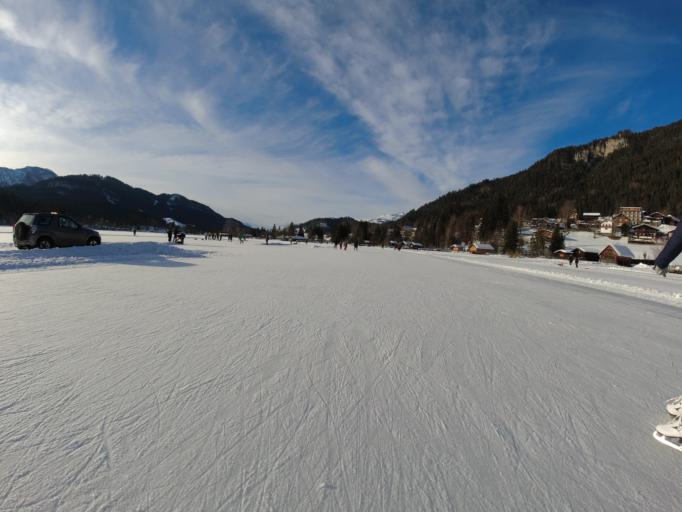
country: AT
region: Carinthia
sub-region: Politischer Bezirk Spittal an der Drau
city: Steinfeld
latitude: 46.7199
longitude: 13.2730
